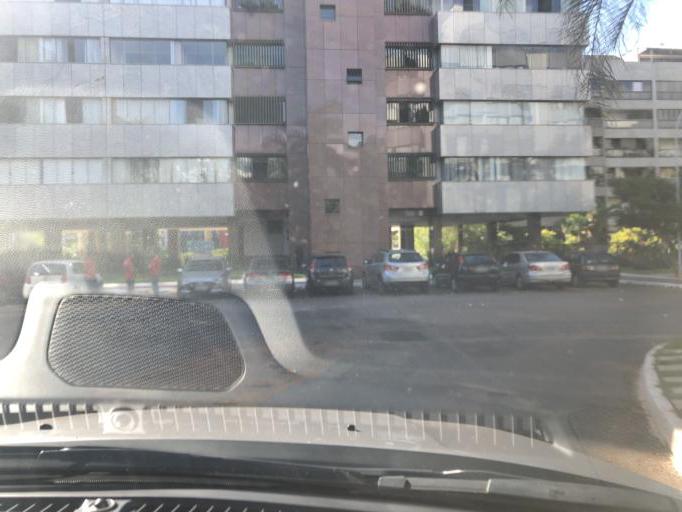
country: BR
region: Federal District
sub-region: Brasilia
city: Brasilia
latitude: -15.8012
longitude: -47.9219
